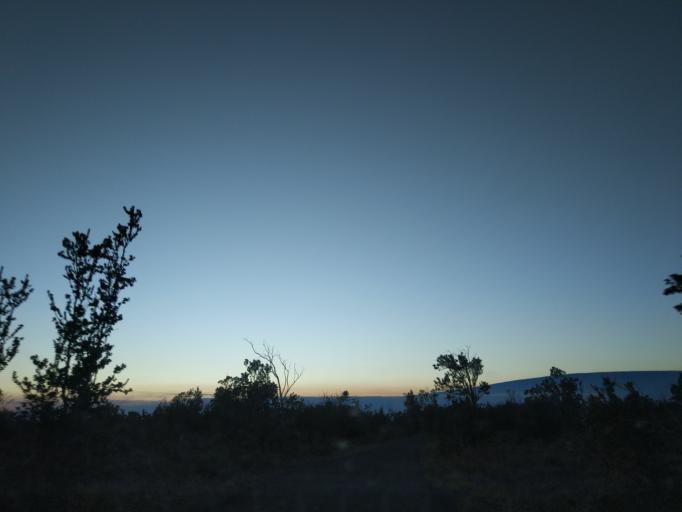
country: US
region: Hawaii
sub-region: Hawaii County
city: Volcano
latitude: 19.3455
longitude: -155.2655
